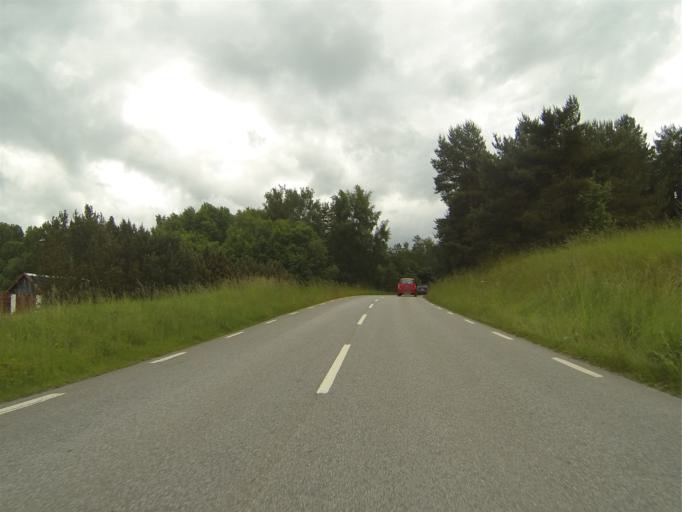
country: SE
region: Skane
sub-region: Lunds Kommun
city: Genarp
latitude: 55.6750
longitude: 13.4127
